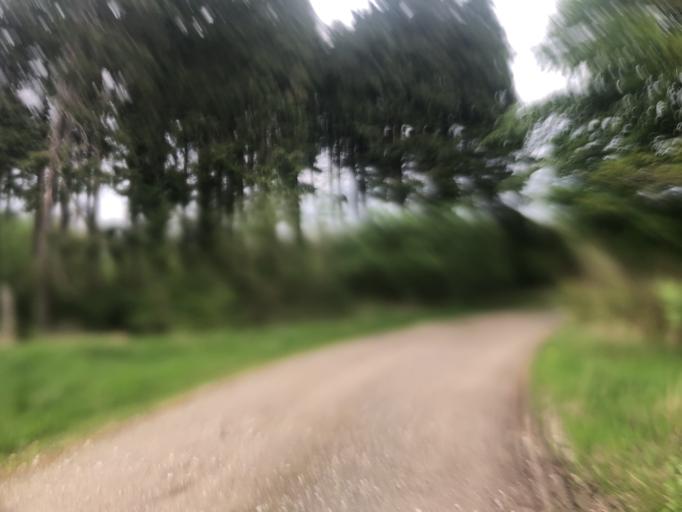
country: DK
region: Zealand
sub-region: Koge Kommune
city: Ejby
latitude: 55.4450
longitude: 12.0918
